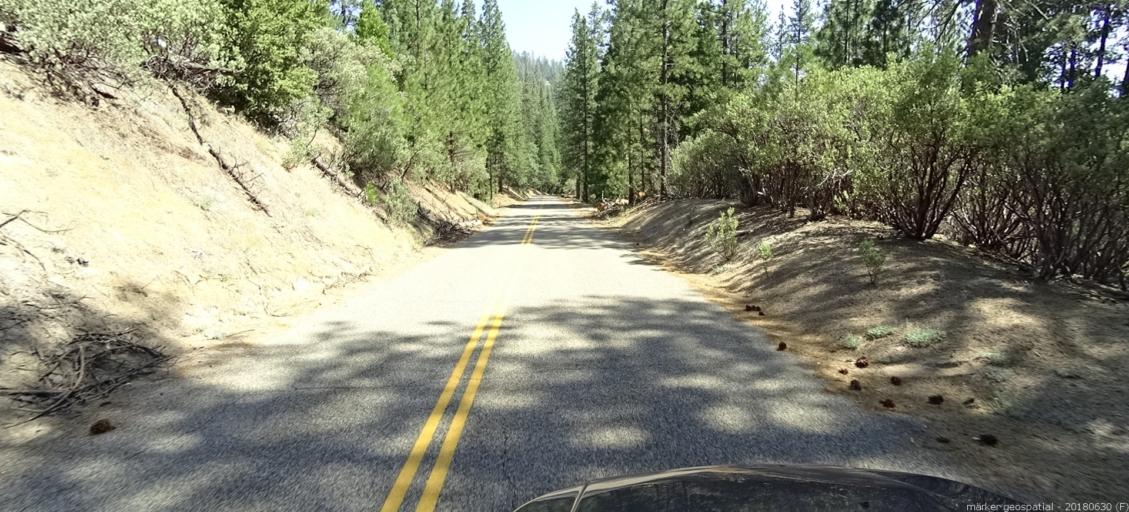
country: US
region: California
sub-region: Madera County
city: Oakhurst
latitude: 37.3789
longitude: -119.3741
